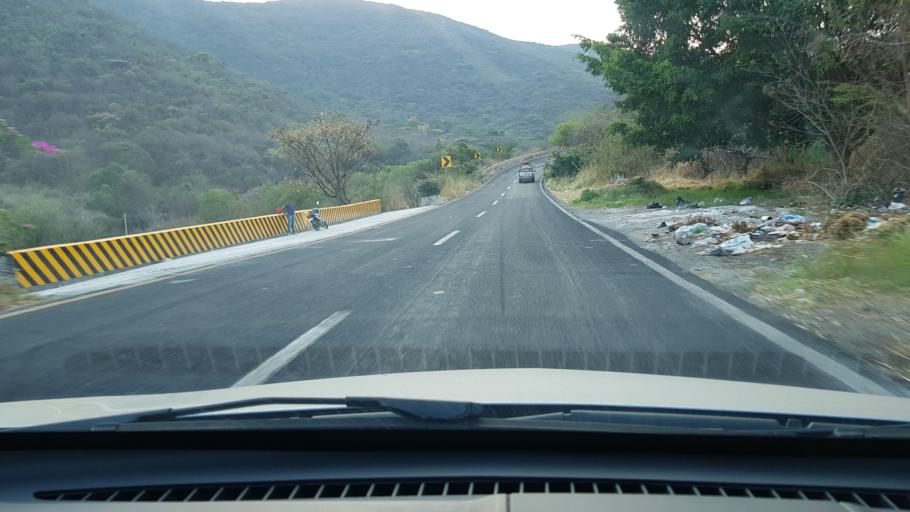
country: MX
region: Morelos
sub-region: Jiutepec
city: Independencia
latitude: 18.8565
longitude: -99.1128
